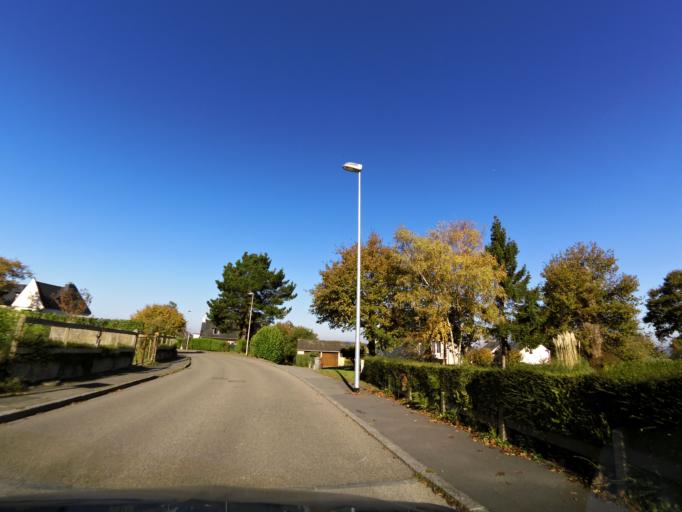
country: FR
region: Brittany
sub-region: Departement d'Ille-et-Vilaine
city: Bain-de-Bretagne
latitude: 47.8483
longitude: -1.6864
